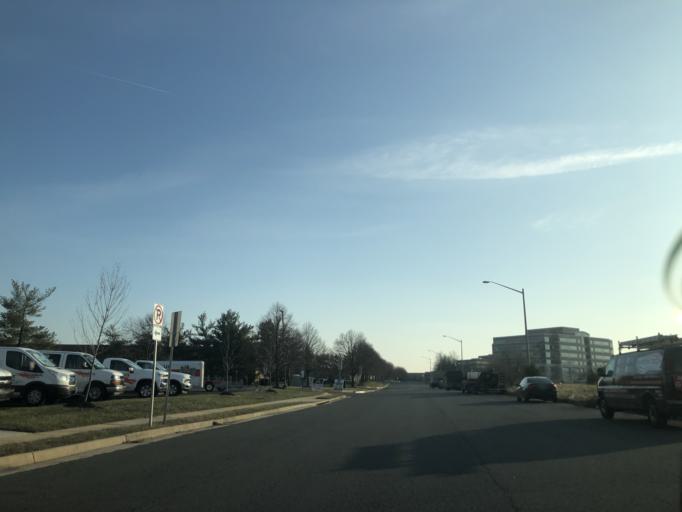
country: US
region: Virginia
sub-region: Fairfax County
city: Floris
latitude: 38.9398
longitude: -77.4277
